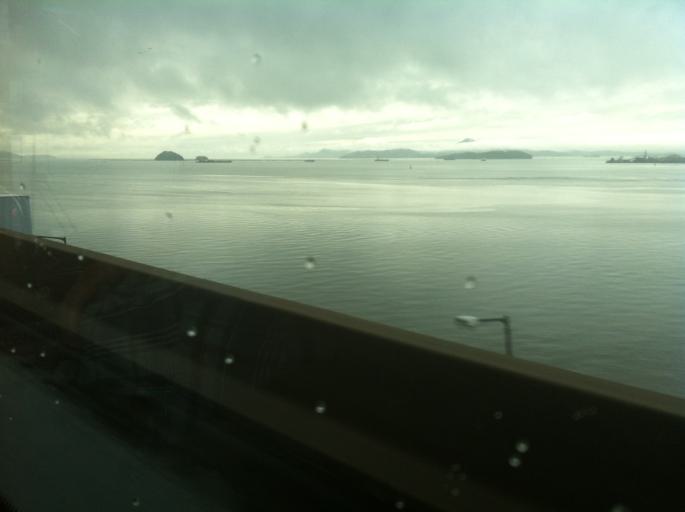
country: KR
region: Incheon
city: Incheon
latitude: 37.5522
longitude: 126.6043
